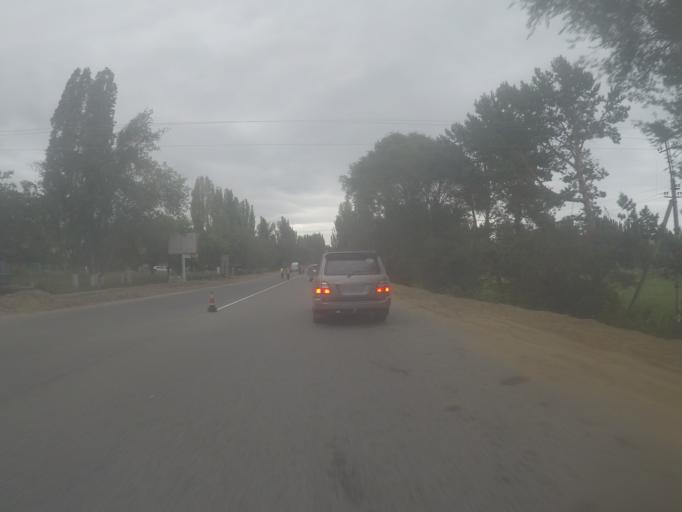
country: KG
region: Ysyk-Koel
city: Cholpon-Ata
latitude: 42.6746
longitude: 77.2994
